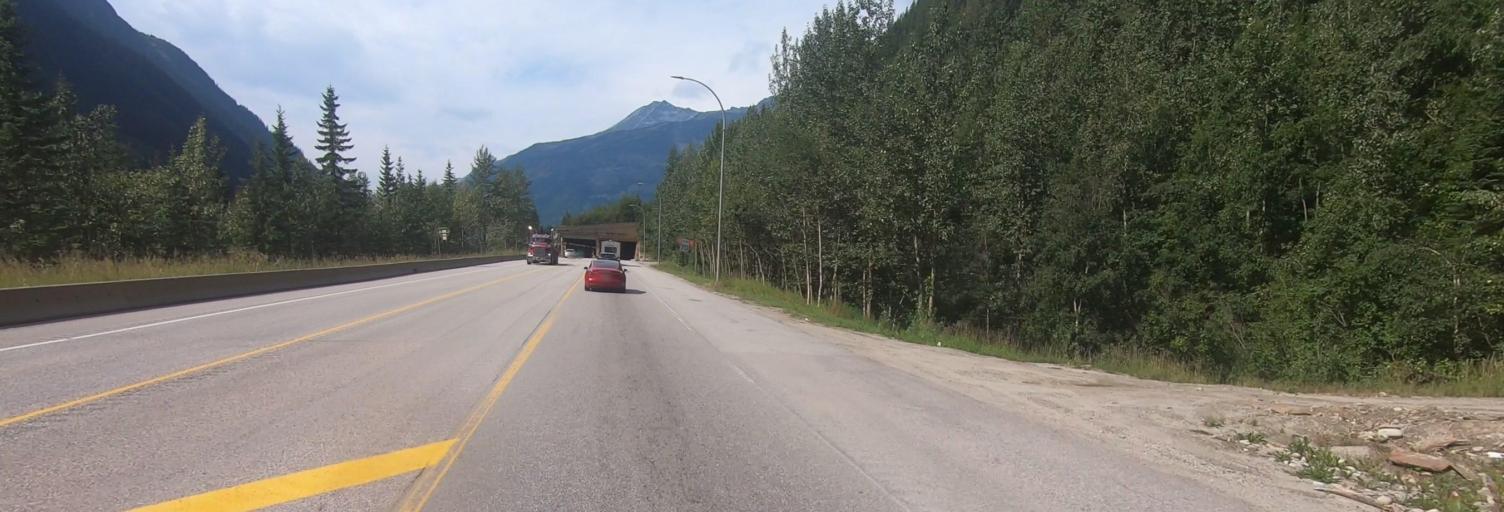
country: CA
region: British Columbia
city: Golden
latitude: 51.3296
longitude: -117.4647
